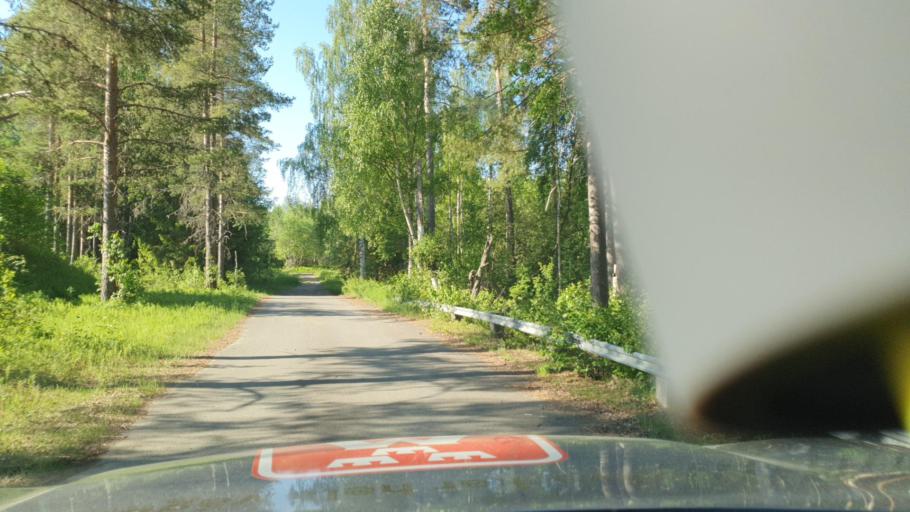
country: SE
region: Norrbotten
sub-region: Alvsbyns Kommun
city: AElvsbyn
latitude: 66.2222
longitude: 20.8603
